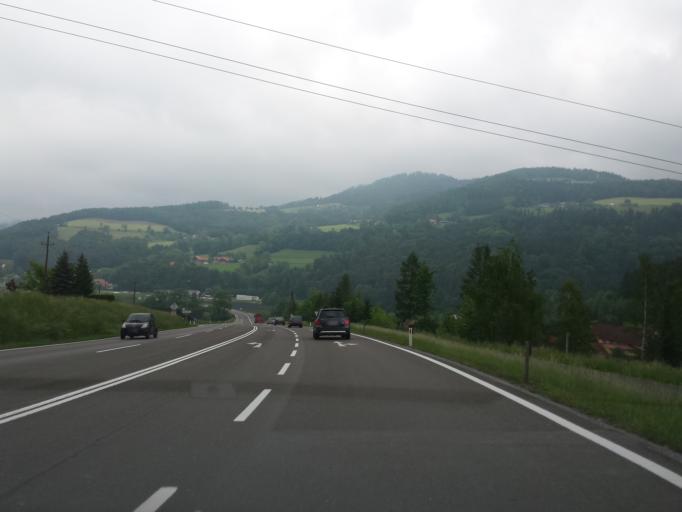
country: AT
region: Styria
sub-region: Politischer Bezirk Weiz
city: Anger
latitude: 47.2531
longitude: 15.7126
